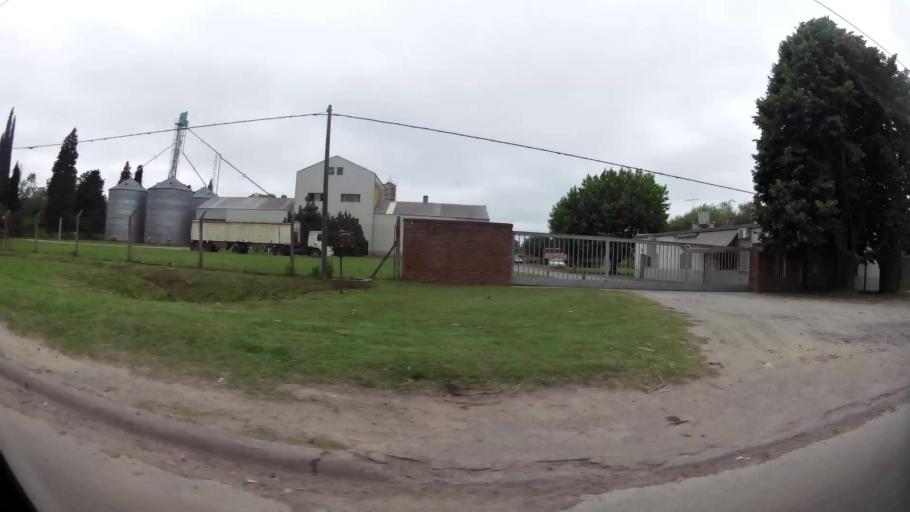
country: AR
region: Buenos Aires
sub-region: Partido de La Plata
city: La Plata
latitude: -34.9664
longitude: -58.0163
